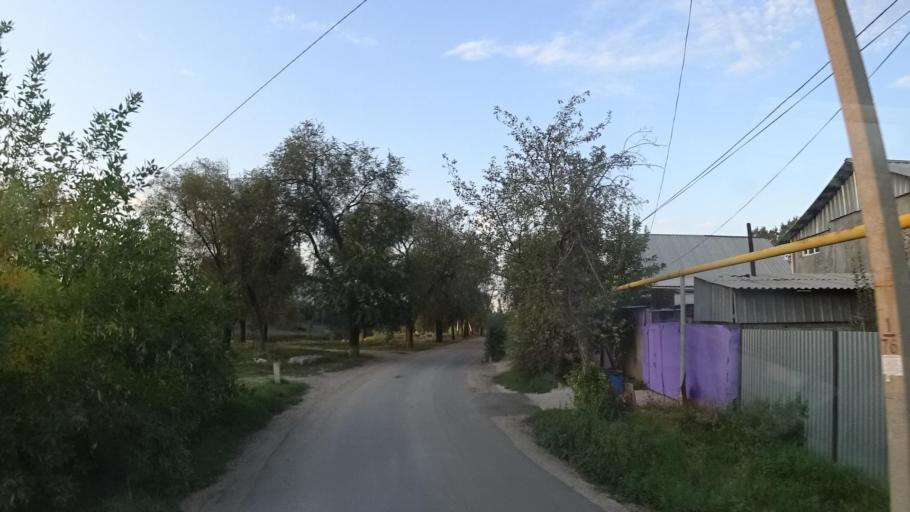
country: KZ
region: Almaty Oblysy
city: Pervomayskiy
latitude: 43.3375
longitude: 76.9937
